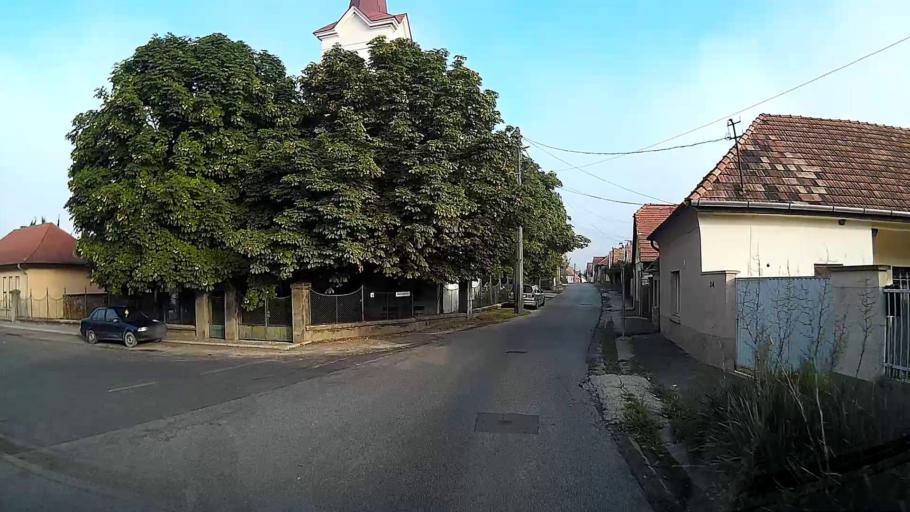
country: HU
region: Pest
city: Tahitotfalu
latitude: 47.7535
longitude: 19.0916
